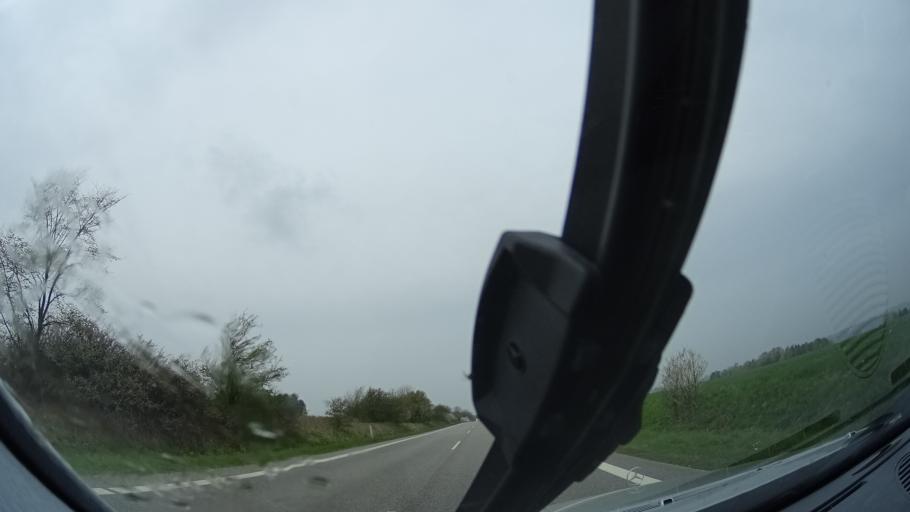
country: DK
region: Zealand
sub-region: Holbaek Kommune
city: Holbaek
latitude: 55.7182
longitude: 11.6455
